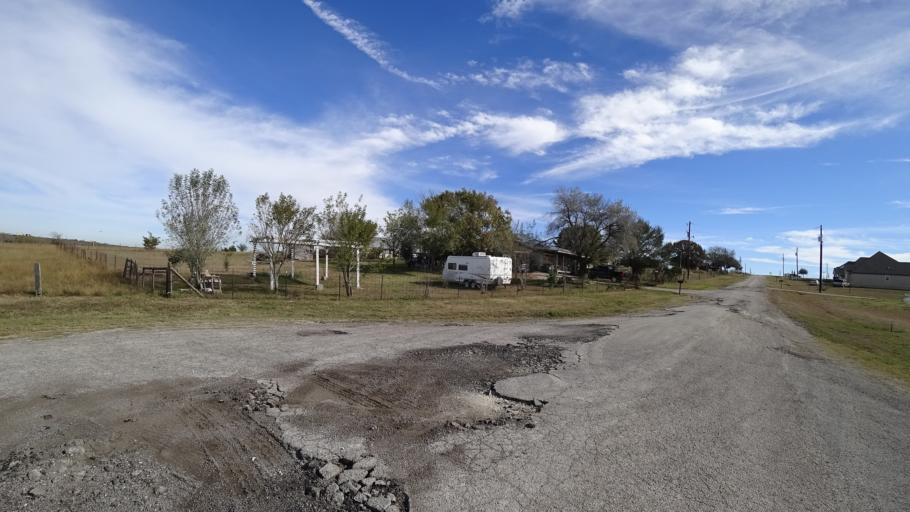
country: US
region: Texas
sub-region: Travis County
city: Onion Creek
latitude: 30.1268
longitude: -97.6941
